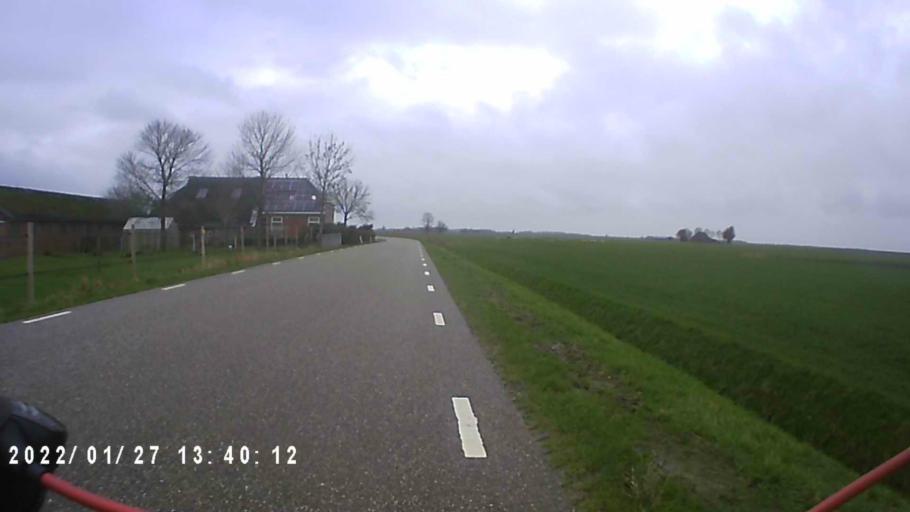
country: NL
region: Friesland
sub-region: Gemeente Kollumerland en Nieuwkruisland
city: Kollum
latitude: 53.2997
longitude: 6.2184
